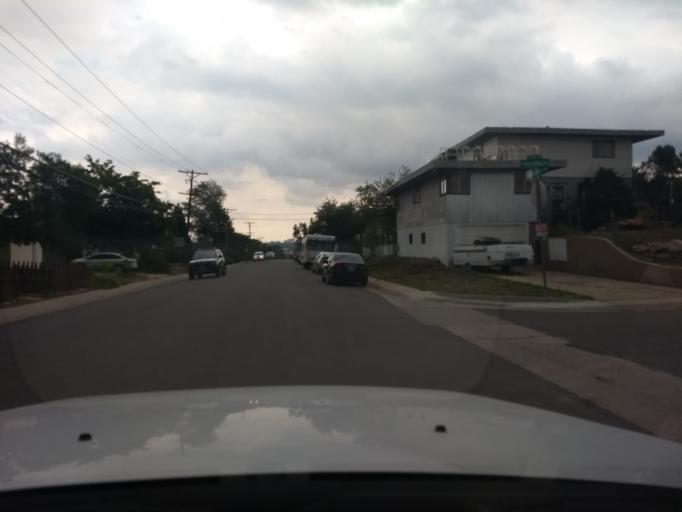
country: US
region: Colorado
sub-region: Denver County
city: Denver
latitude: 39.7040
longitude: -105.0123
